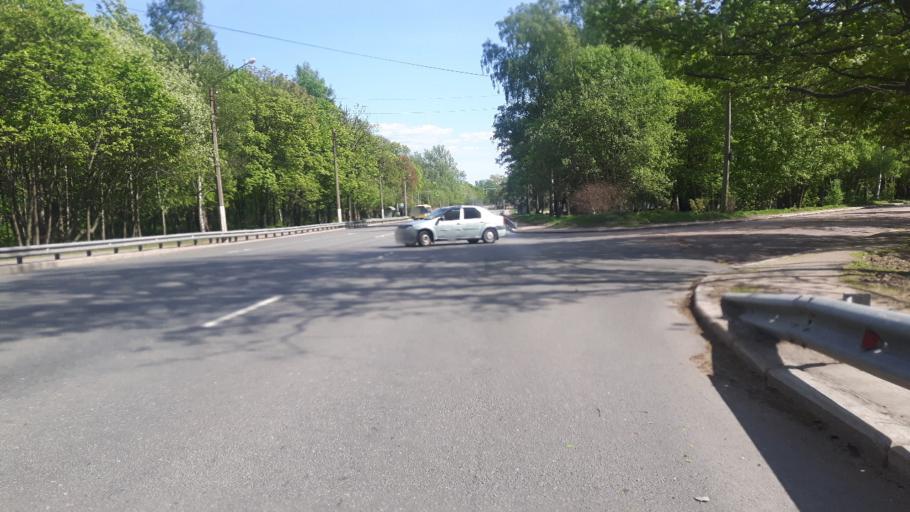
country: RU
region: Leningrad
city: Vyborg
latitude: 60.7291
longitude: 28.7008
